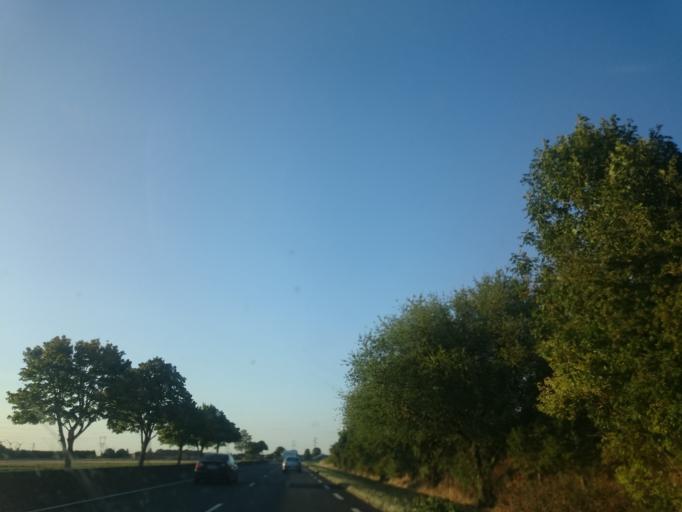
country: FR
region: Ile-de-France
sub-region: Departement de l'Essonne
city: Angerville
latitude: 48.3108
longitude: 1.9928
